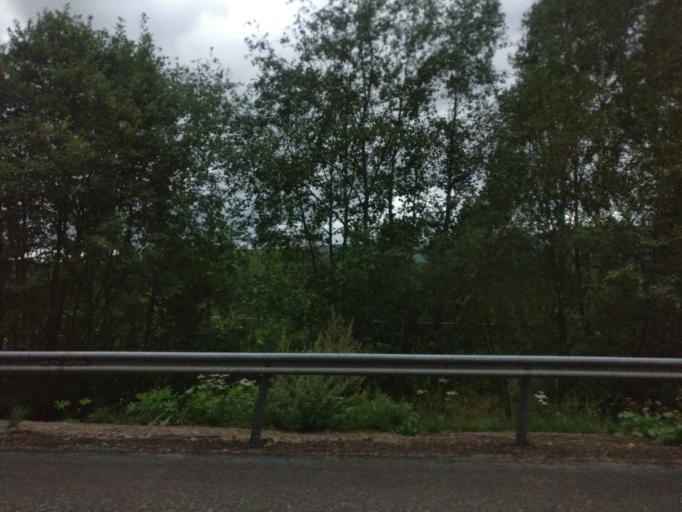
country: SE
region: Vaermland
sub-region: Torsby Kommun
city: Torsby
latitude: 60.6430
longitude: 13.0057
